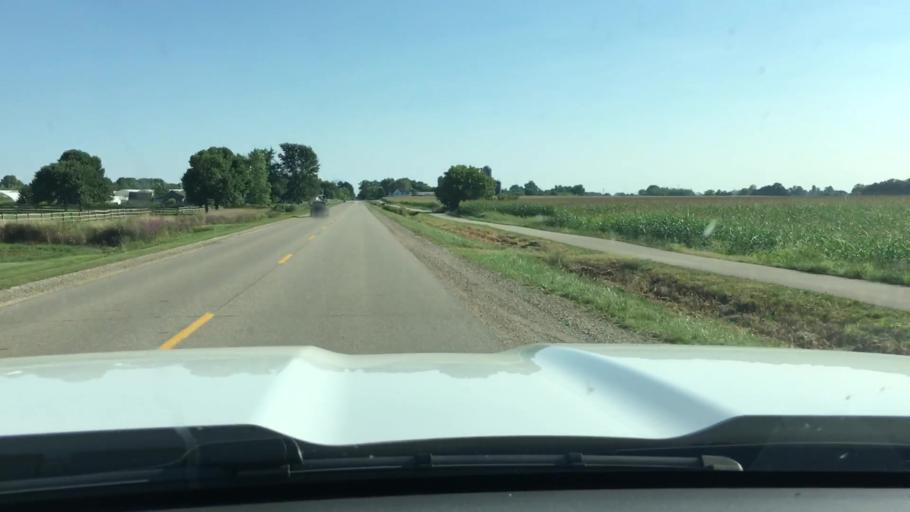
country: US
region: Michigan
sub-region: Ottawa County
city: Zeeland
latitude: 42.7932
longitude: -85.9403
